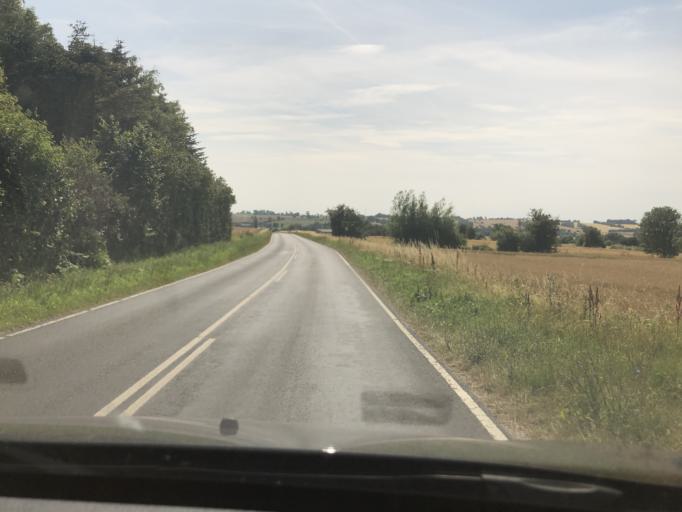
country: DK
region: South Denmark
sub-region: AEro Kommune
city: AEroskobing
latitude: 54.8798
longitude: 10.4014
